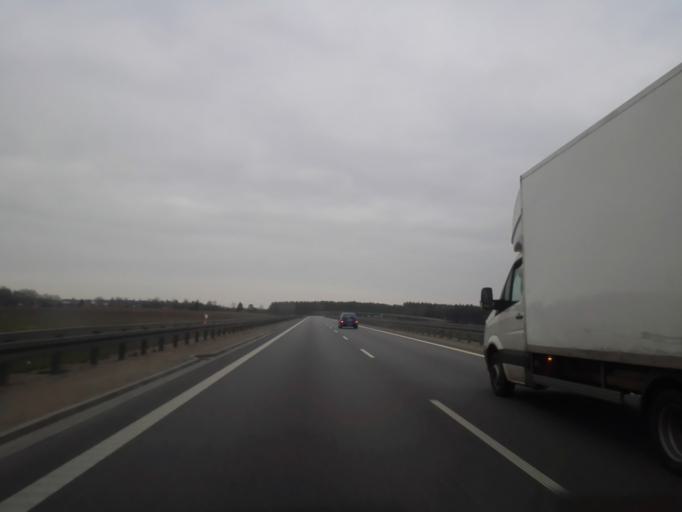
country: PL
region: Podlasie
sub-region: Powiat kolnenski
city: Stawiski
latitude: 53.3693
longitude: 22.1510
